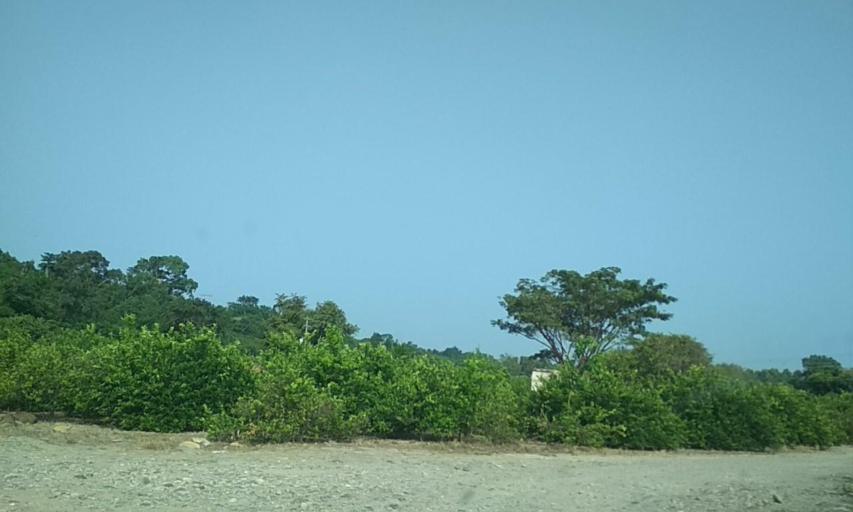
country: MX
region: Veracruz
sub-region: Misantla
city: La Defensa
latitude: 20.0503
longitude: -96.9818
